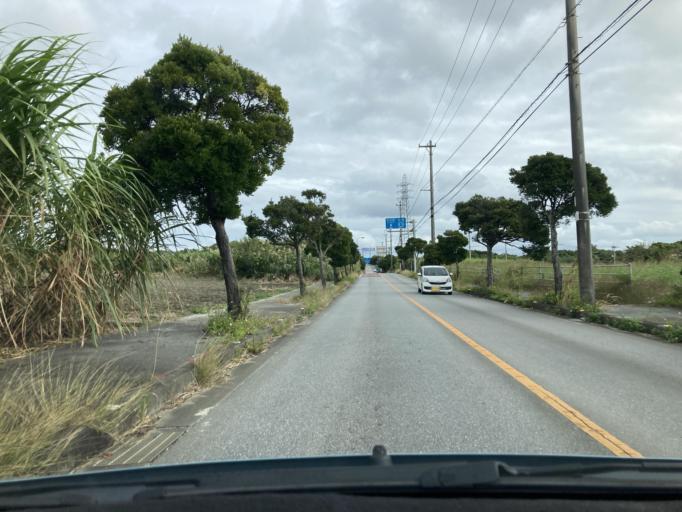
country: JP
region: Okinawa
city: Itoman
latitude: 26.1194
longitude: 127.6863
